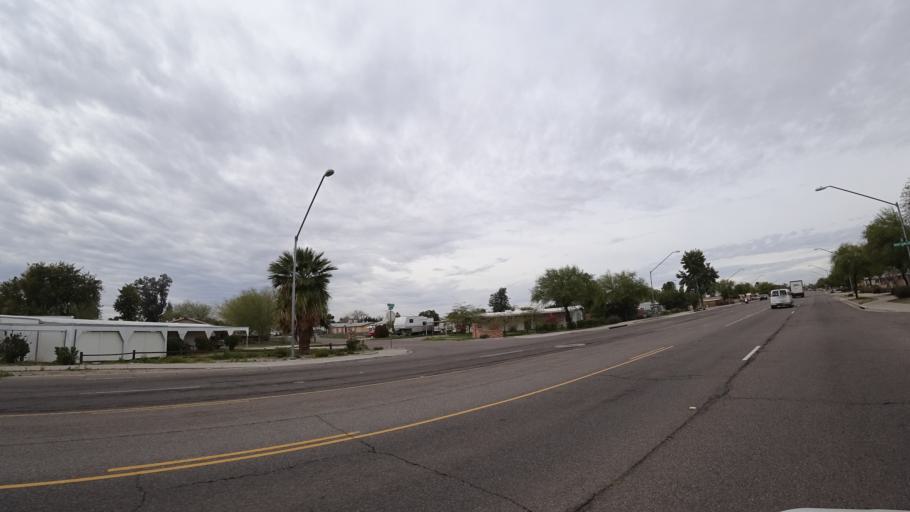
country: US
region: Arizona
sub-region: Maricopa County
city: Peoria
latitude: 33.6269
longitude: -112.2024
